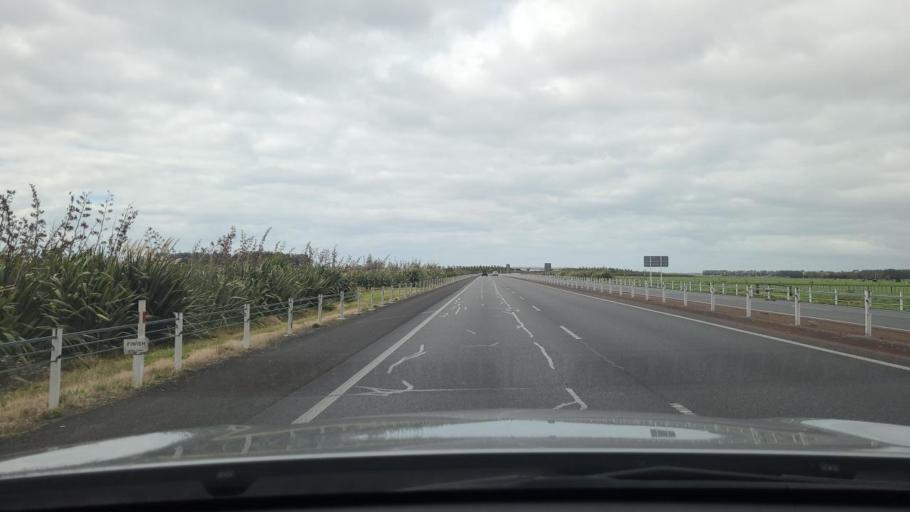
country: NZ
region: Bay of Plenty
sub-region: Tauranga City
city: Tauranga
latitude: -37.7190
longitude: 176.2976
